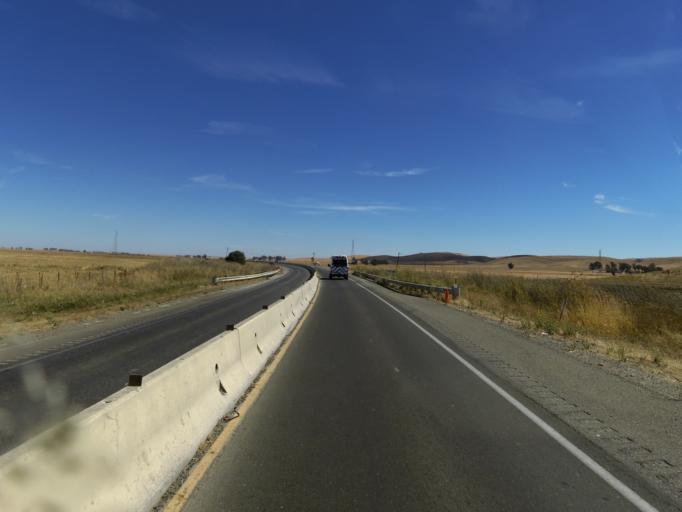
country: US
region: California
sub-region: Solano County
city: Suisun
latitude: 38.2300
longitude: -121.9769
